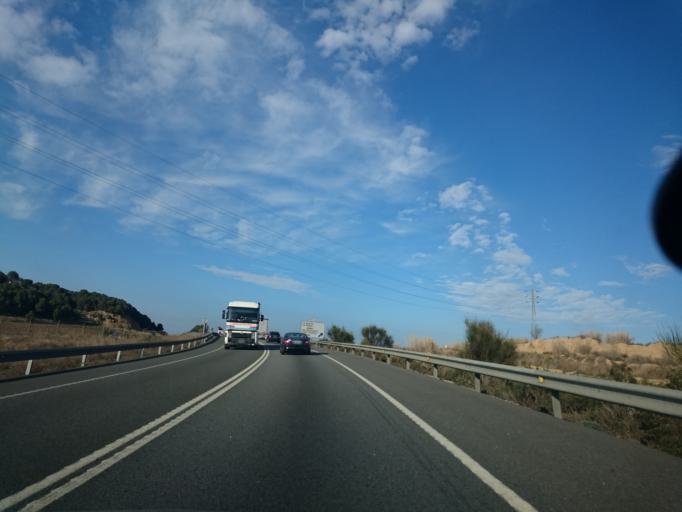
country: ES
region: Catalonia
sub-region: Provincia de Barcelona
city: Castellet
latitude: 41.2976
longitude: 1.6324
